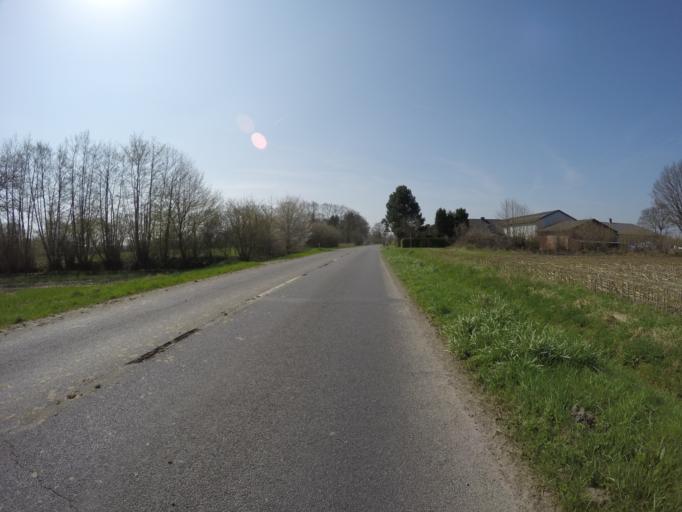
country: DE
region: Schleswig-Holstein
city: Quickborn
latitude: 53.7129
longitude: 9.8842
